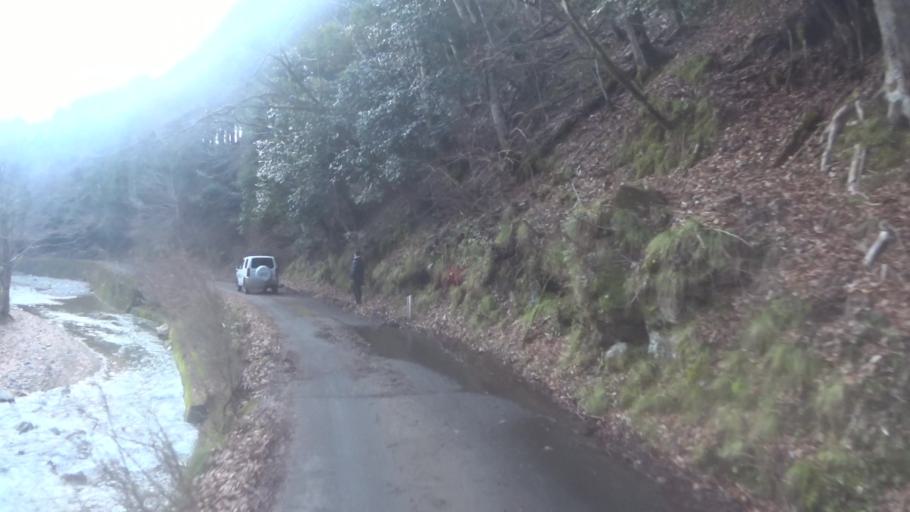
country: JP
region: Kyoto
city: Maizuru
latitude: 35.3991
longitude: 135.4869
